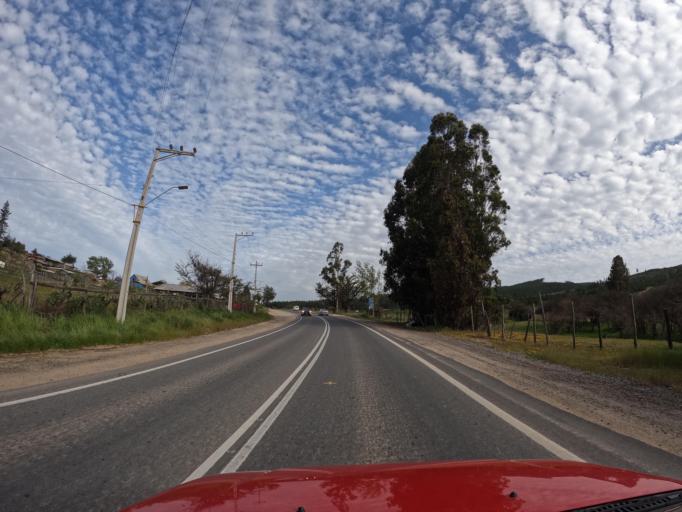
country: CL
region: O'Higgins
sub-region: Provincia de Colchagua
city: Santa Cruz
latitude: -34.3181
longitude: -71.7626
